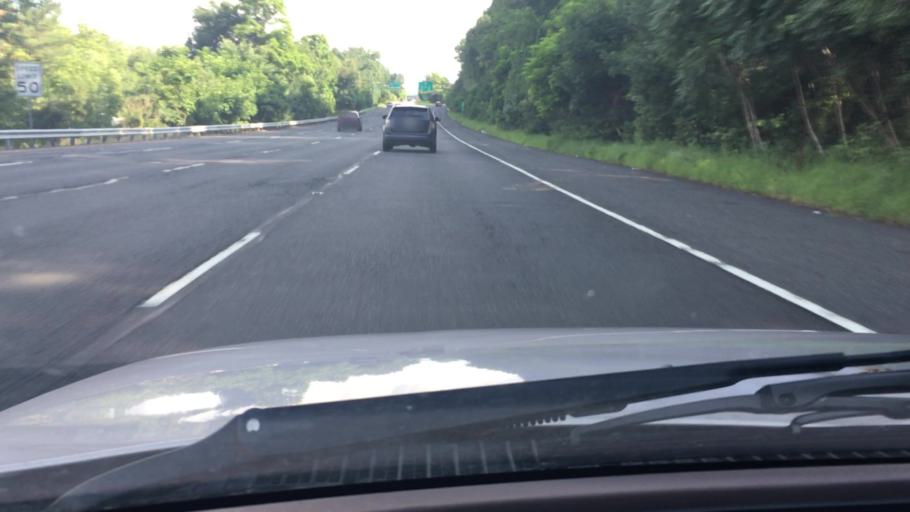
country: US
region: New Jersey
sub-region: Passaic County
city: Woodland Park
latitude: 40.8870
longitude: -74.1682
